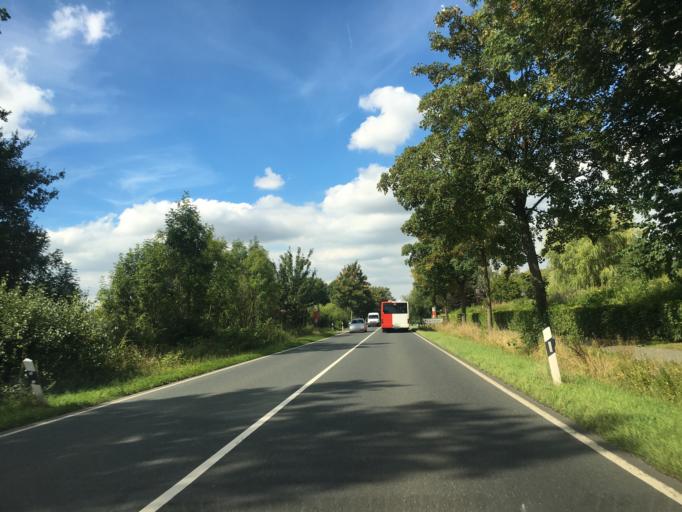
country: DE
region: North Rhine-Westphalia
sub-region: Regierungsbezirk Detmold
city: Barntrup
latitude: 51.9830
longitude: 9.1363
